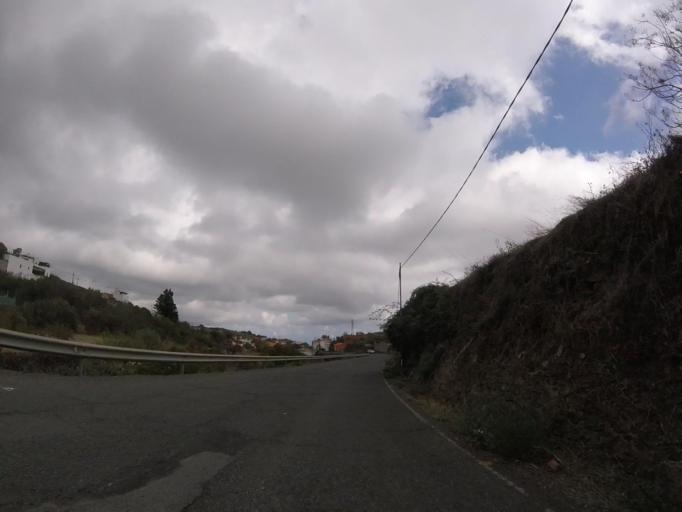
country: ES
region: Canary Islands
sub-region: Provincia de Las Palmas
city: Vega de San Mateo
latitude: 27.9885
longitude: -15.5693
